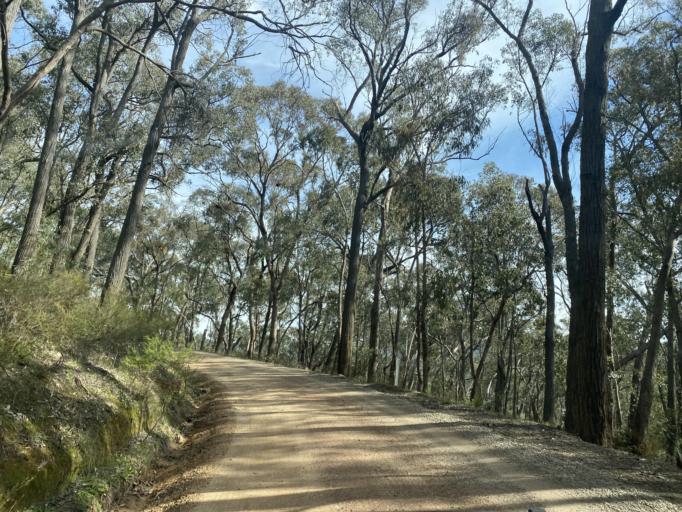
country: AU
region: Victoria
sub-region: Mansfield
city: Mansfield
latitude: -36.8262
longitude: 146.1524
